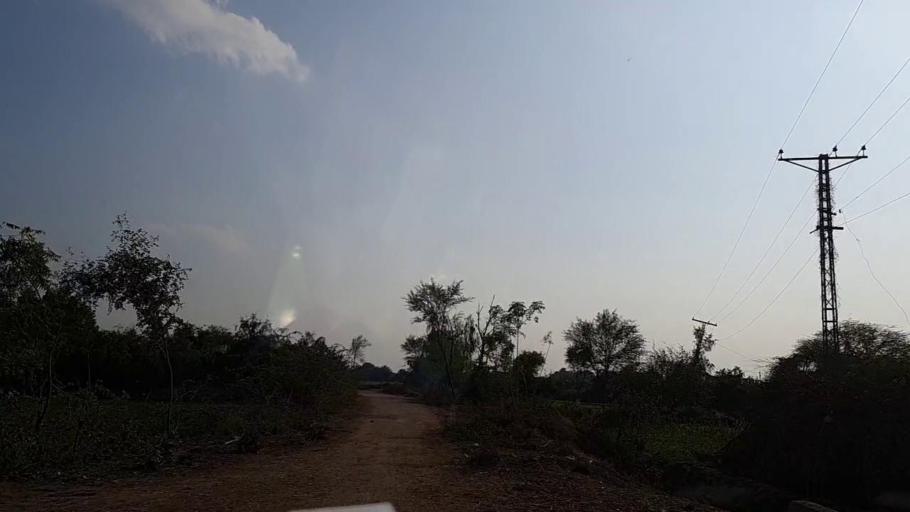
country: PK
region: Sindh
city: Nawabshah
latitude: 26.1441
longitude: 68.3894
